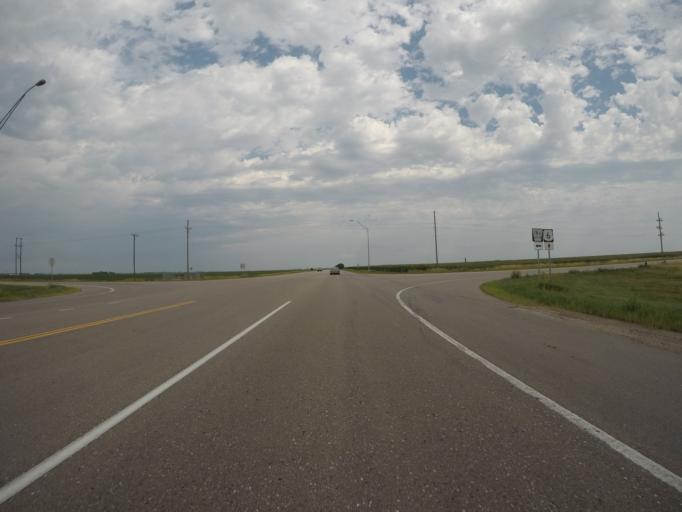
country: US
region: Nebraska
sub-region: Clay County
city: Harvard
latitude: 40.5826
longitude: -98.1095
